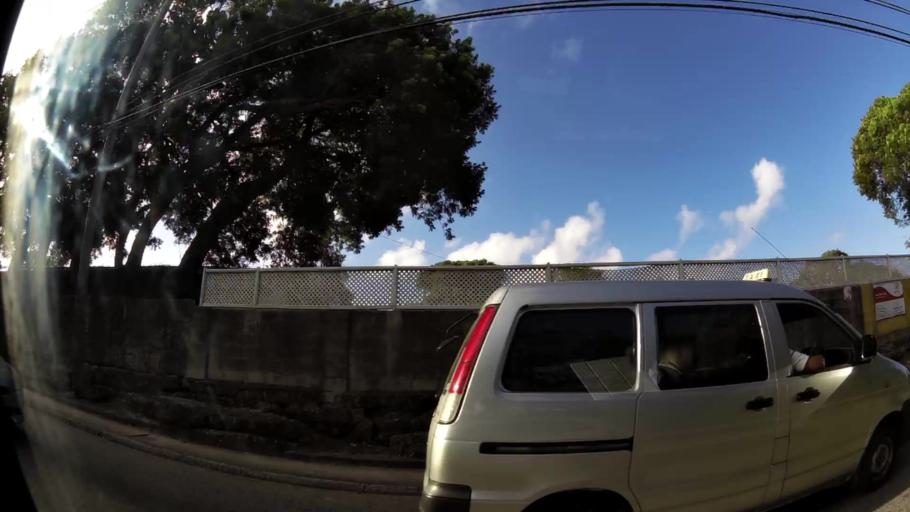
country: BB
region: Saint Michael
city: Bridgetown
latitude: 13.0923
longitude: -59.5902
